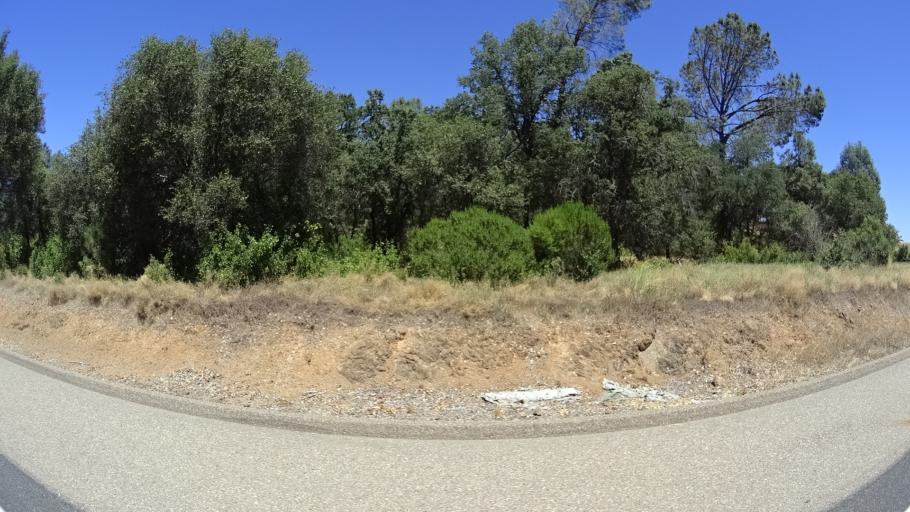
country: US
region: California
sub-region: Calaveras County
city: San Andreas
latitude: 38.1780
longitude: -120.6802
